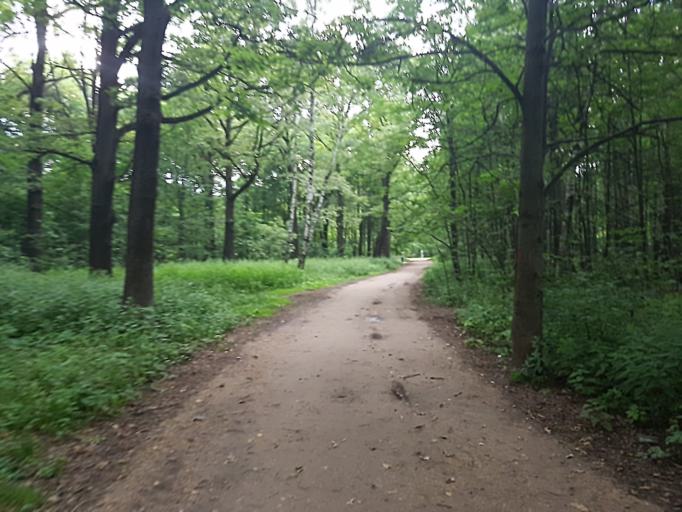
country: RU
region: Moskovskaya
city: Novogireyevo
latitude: 55.7649
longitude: 37.8056
